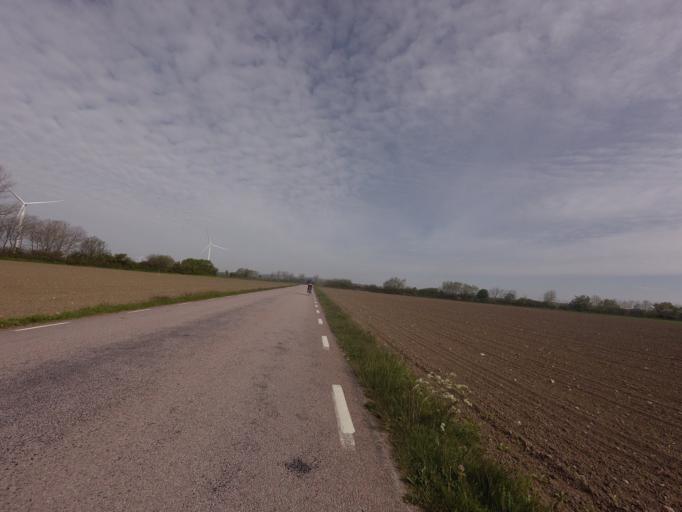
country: SE
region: Skane
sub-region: Hoganas Kommun
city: Hoganas
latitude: 56.2293
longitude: 12.5875
